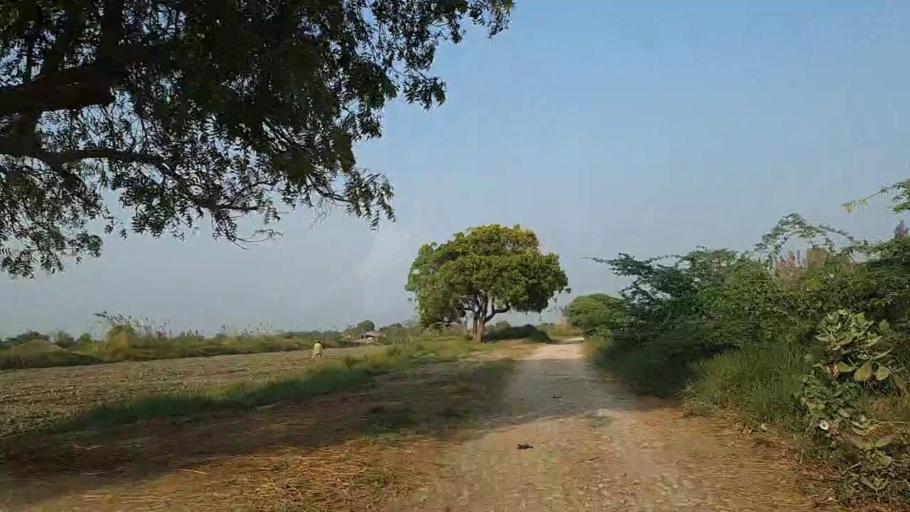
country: PK
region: Sindh
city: Thatta
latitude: 24.6665
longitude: 67.7794
